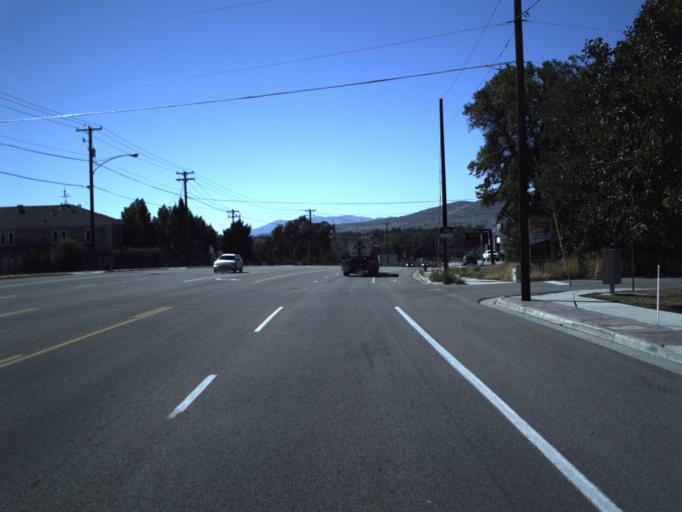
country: US
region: Utah
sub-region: Salt Lake County
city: Bluffdale
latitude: 40.4937
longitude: -111.9389
